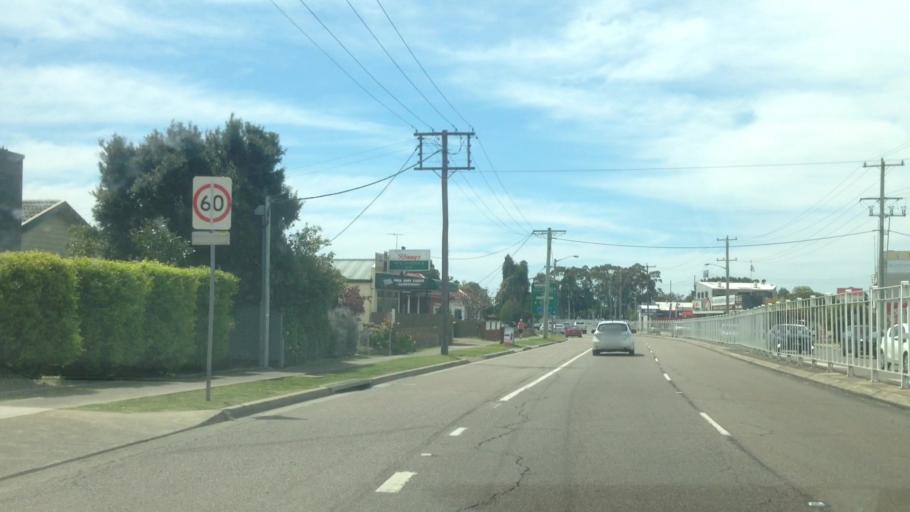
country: AU
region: New South Wales
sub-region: Newcastle
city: Broadmeadow
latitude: -32.9178
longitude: 151.7246
